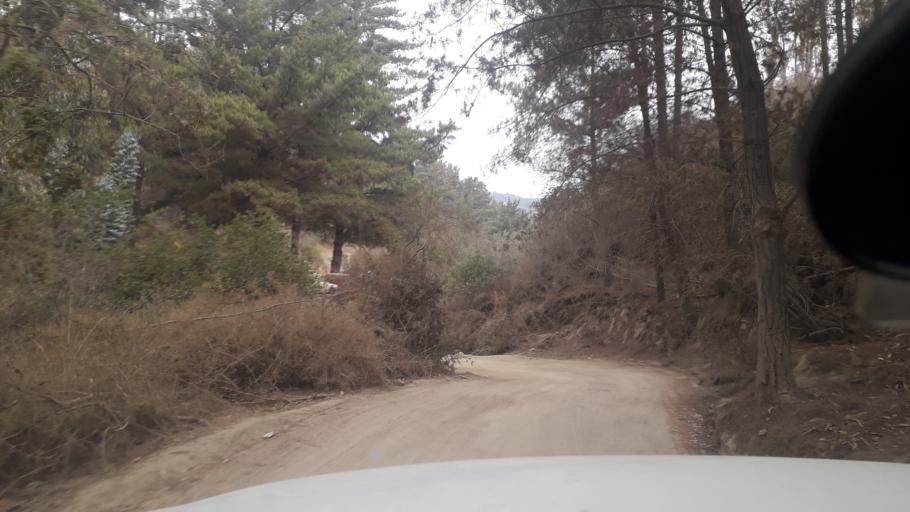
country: CL
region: Valparaiso
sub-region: Provincia de Valparaiso
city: Valparaiso
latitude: -33.1160
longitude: -71.6434
